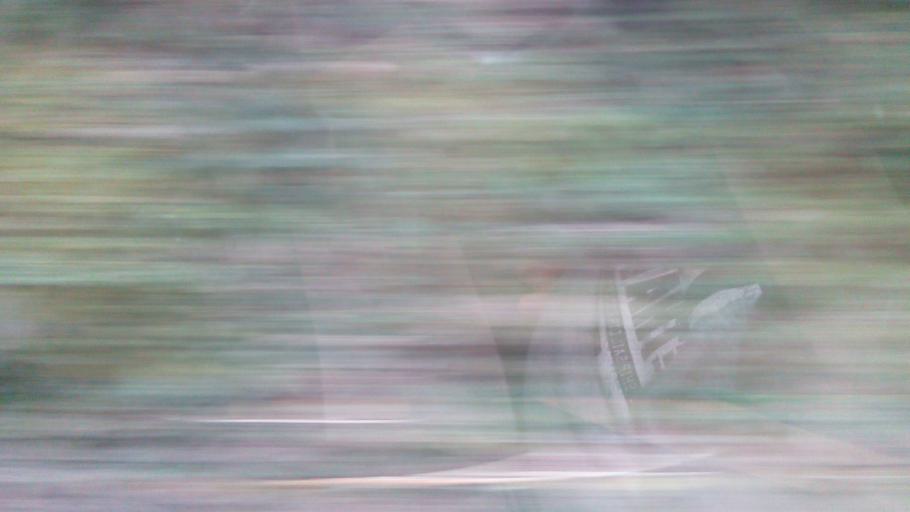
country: TW
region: Taiwan
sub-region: Hualien
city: Hualian
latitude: 24.3682
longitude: 121.3391
